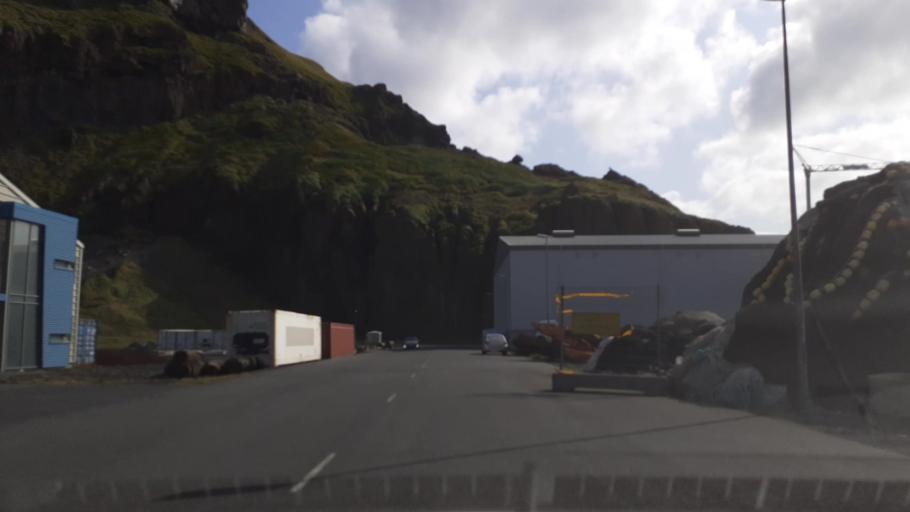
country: IS
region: South
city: Vestmannaeyjar
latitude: 63.4474
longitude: -20.2732
